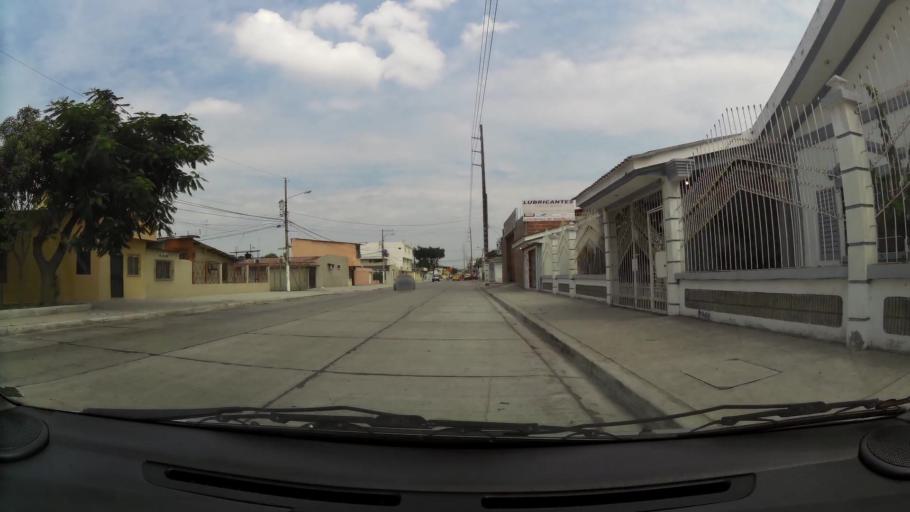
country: EC
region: Guayas
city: Guayaquil
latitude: -2.2426
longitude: -79.9051
